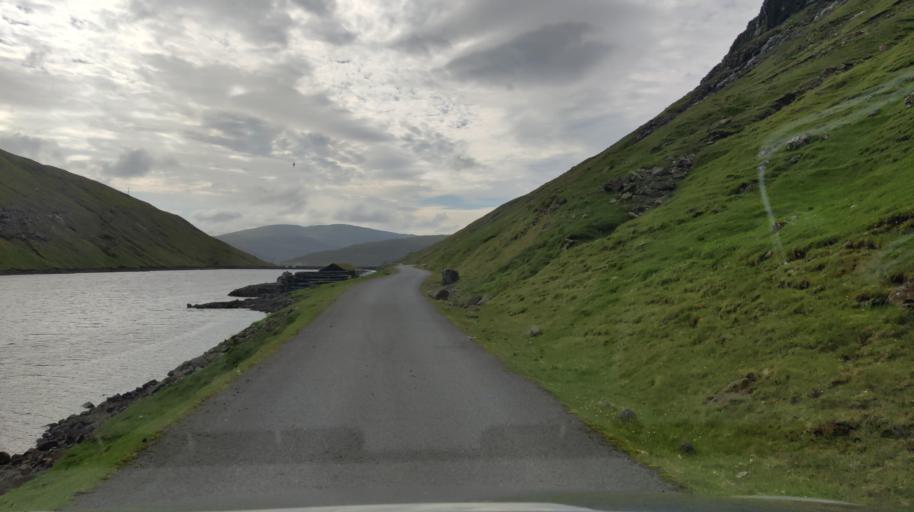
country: FO
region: Streymoy
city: Vestmanna
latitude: 62.1550
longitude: -7.1166
